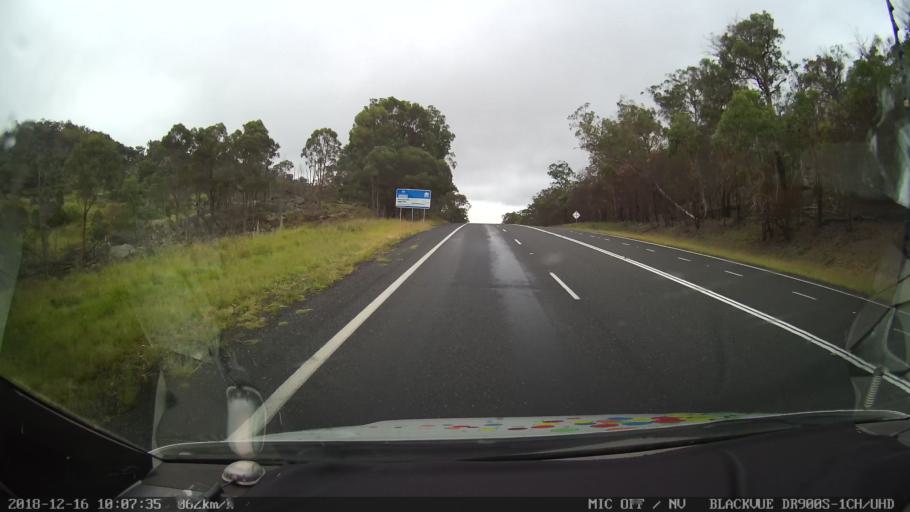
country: AU
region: New South Wales
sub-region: Glen Innes Severn
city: Glen Innes
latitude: -29.3347
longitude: 151.8974
